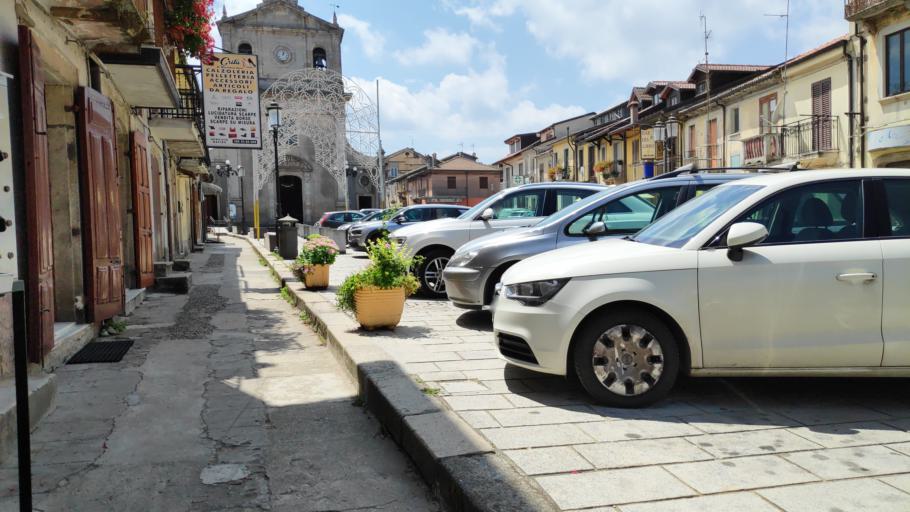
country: IT
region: Calabria
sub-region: Provincia di Vibo-Valentia
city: Serra San Bruno
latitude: 38.5762
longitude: 16.3298
